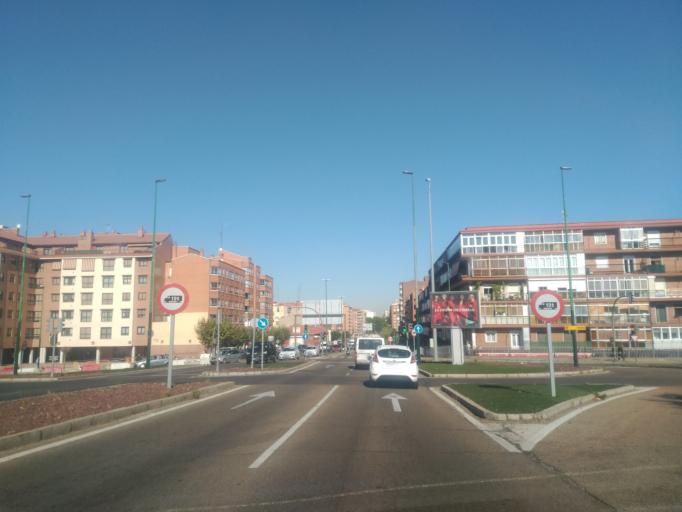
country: ES
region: Castille and Leon
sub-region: Provincia de Valladolid
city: Valladolid
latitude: 41.6421
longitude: -4.7123
